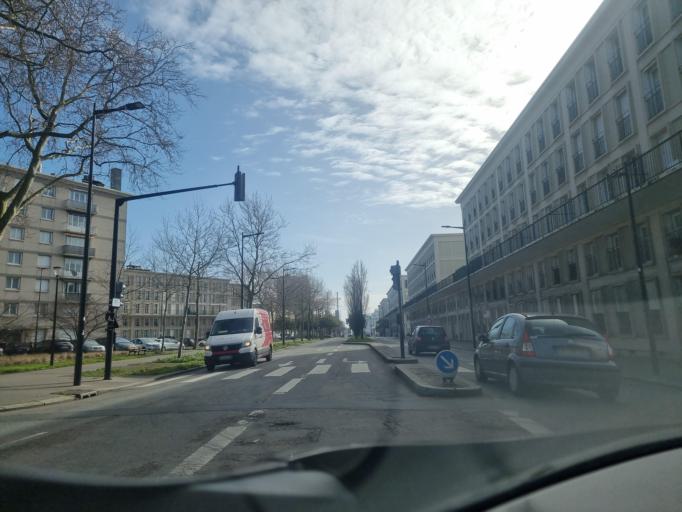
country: FR
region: Haute-Normandie
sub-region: Departement de la Seine-Maritime
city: Le Havre
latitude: 49.4873
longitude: 0.1034
